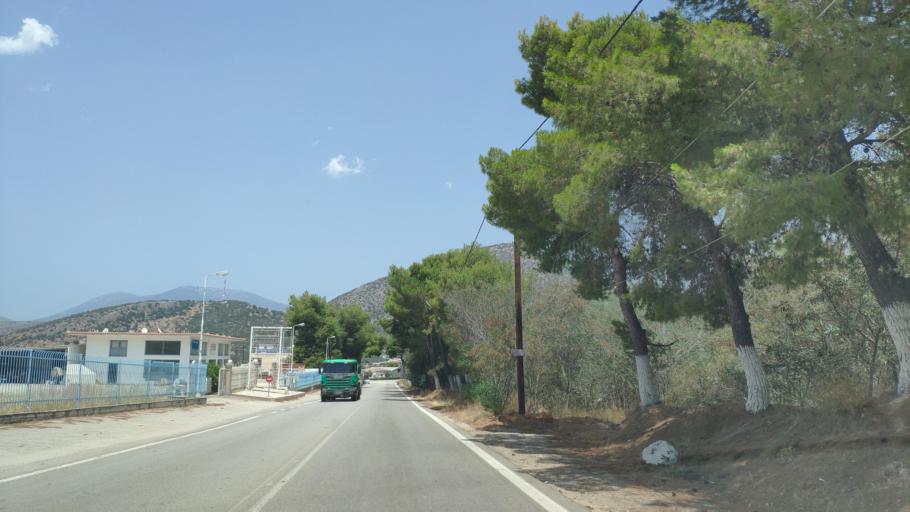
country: GR
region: Peloponnese
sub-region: Nomos Argolidos
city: Kranidi
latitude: 37.3852
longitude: 23.1560
